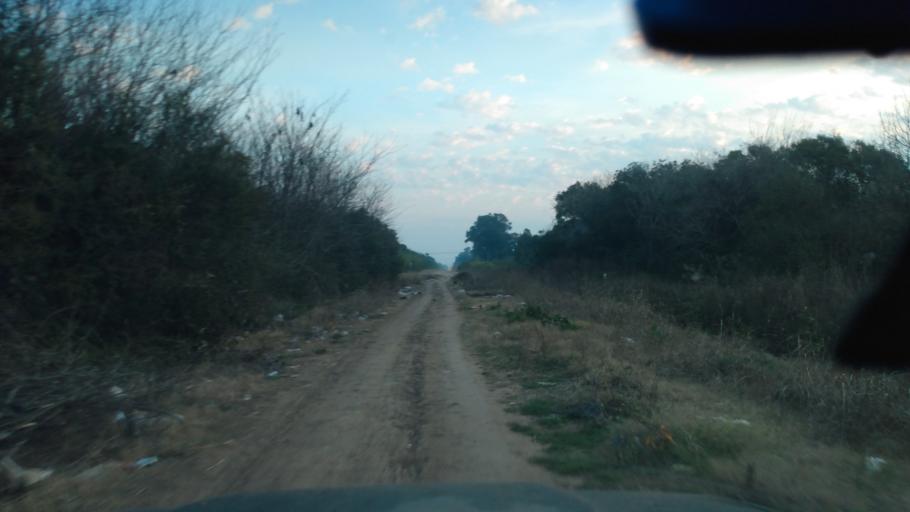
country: AR
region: Buenos Aires
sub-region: Partido de Lujan
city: Lujan
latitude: -34.5514
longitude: -59.1434
